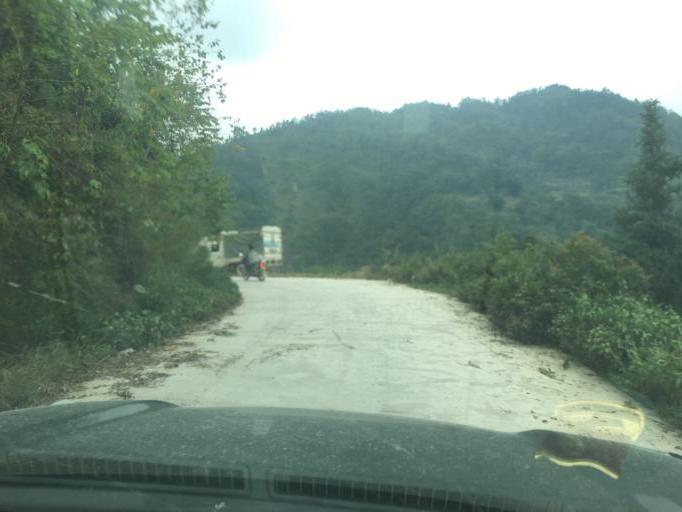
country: CN
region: Guangxi Zhuangzu Zizhiqu
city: Tongle
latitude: 25.3749
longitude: 106.2653
